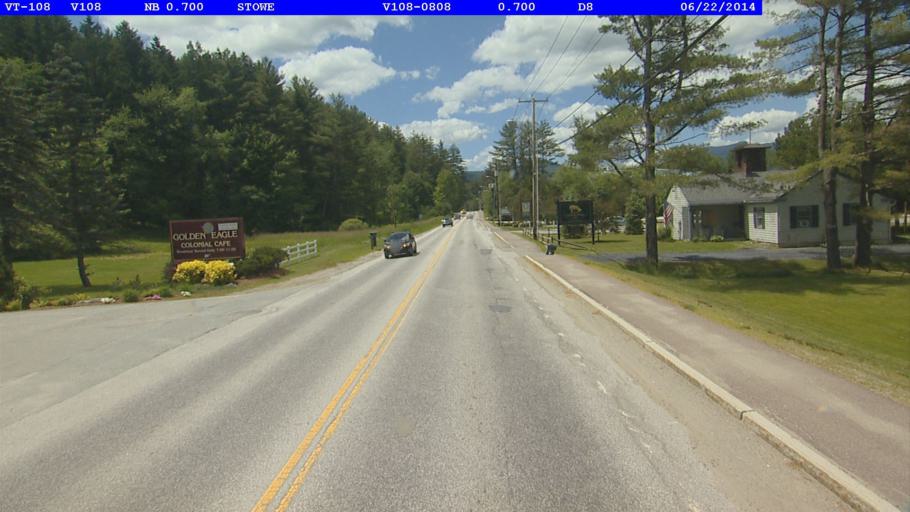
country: US
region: Vermont
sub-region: Lamoille County
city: Morristown
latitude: 44.4732
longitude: -72.6919
